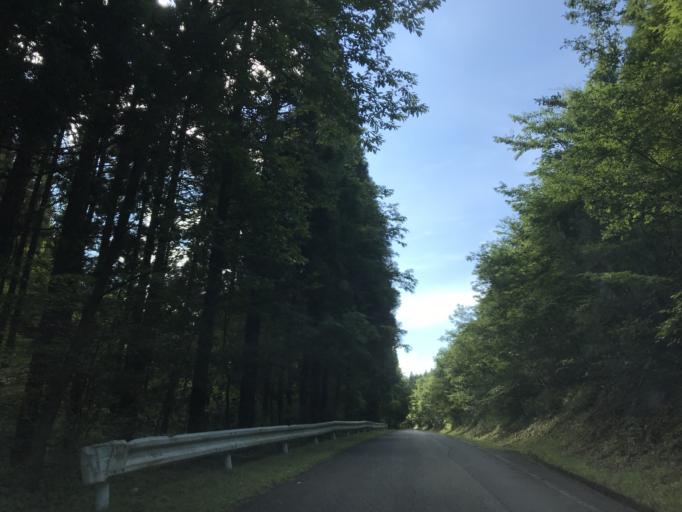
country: JP
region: Iwate
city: Ichinoseki
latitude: 38.9255
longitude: 140.9378
